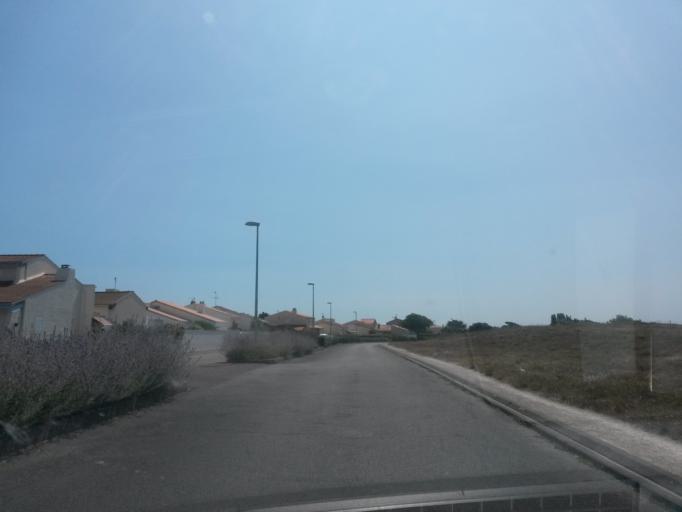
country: FR
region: Pays de la Loire
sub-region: Departement de la Vendee
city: Les Sables-d'Olonne
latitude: 46.5052
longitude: -1.8080
